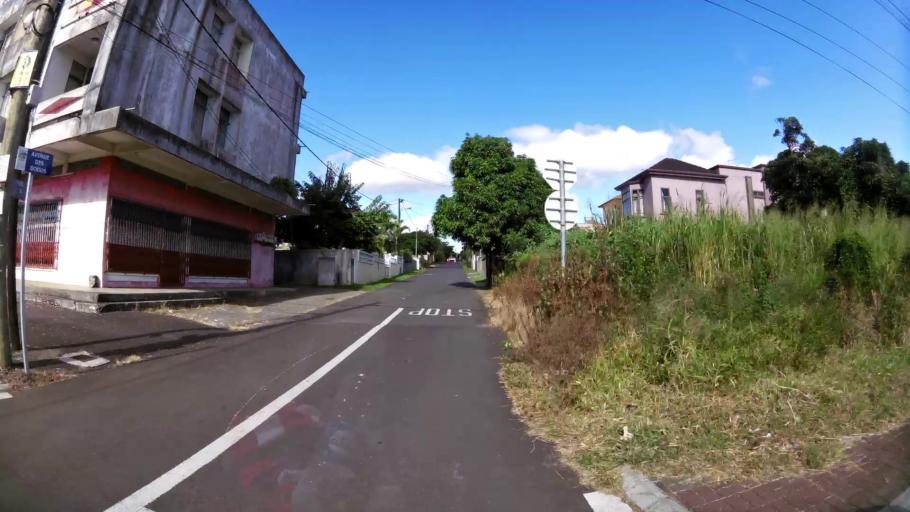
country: MU
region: Plaines Wilhems
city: Quatre Bornes
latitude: -20.2713
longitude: 57.4859
